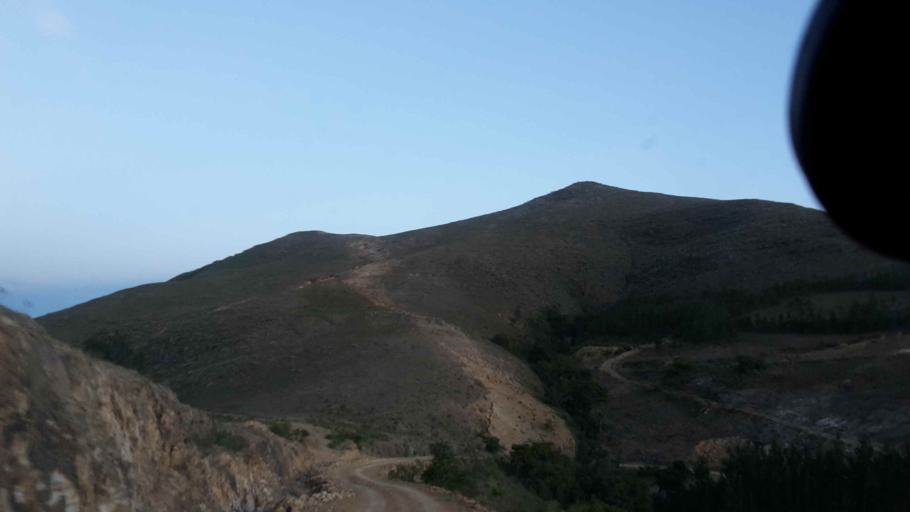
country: BO
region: Cochabamba
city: Mizque
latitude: -17.9154
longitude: -65.5020
